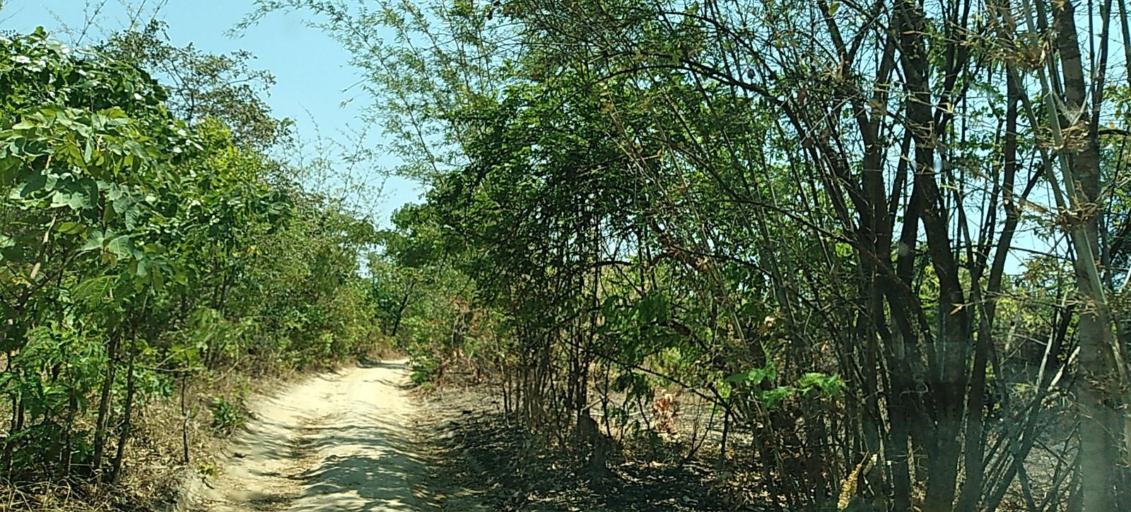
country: ZM
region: Copperbelt
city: Luanshya
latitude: -12.9777
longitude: 28.3303
